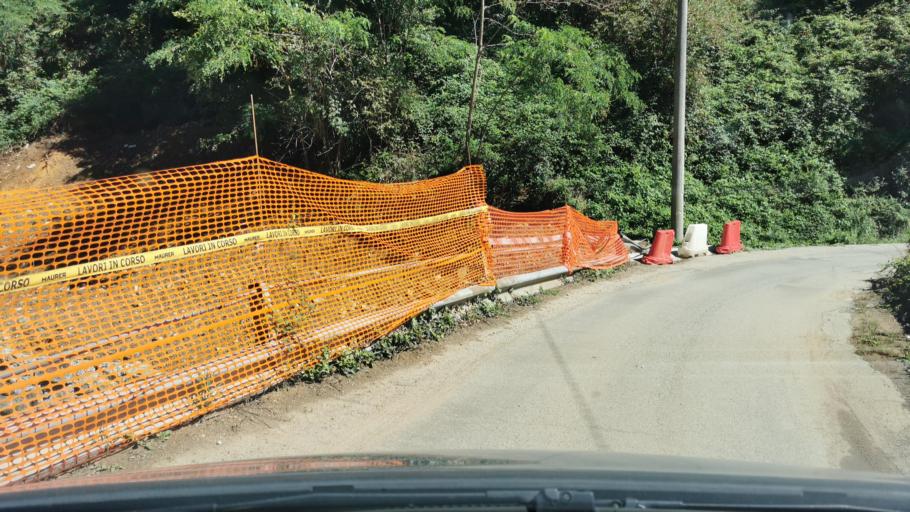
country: IT
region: Piedmont
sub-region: Provincia di Torino
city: Corio
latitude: 45.3119
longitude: 7.5279
